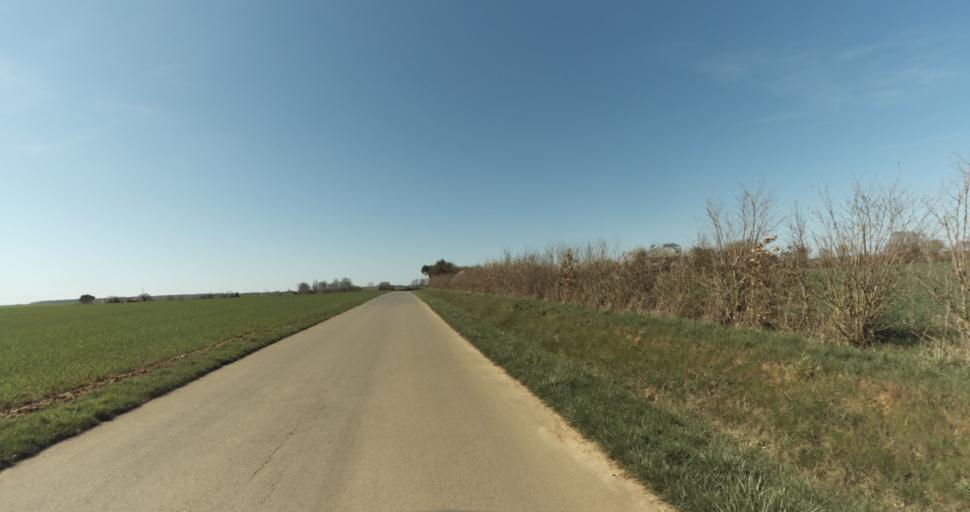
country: FR
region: Lower Normandy
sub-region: Departement du Calvados
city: Canon
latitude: 49.0487
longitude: -0.0598
